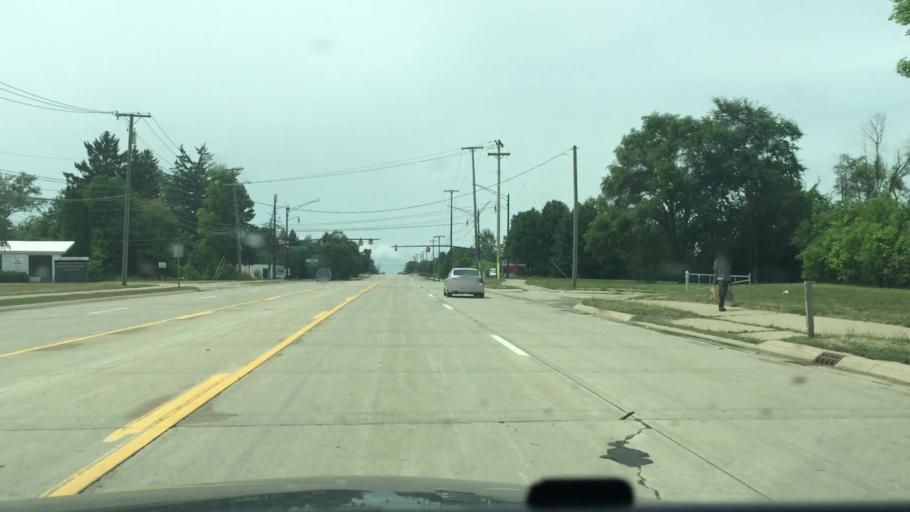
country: US
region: Michigan
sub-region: Oakland County
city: Novi
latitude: 42.4863
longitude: -83.5003
